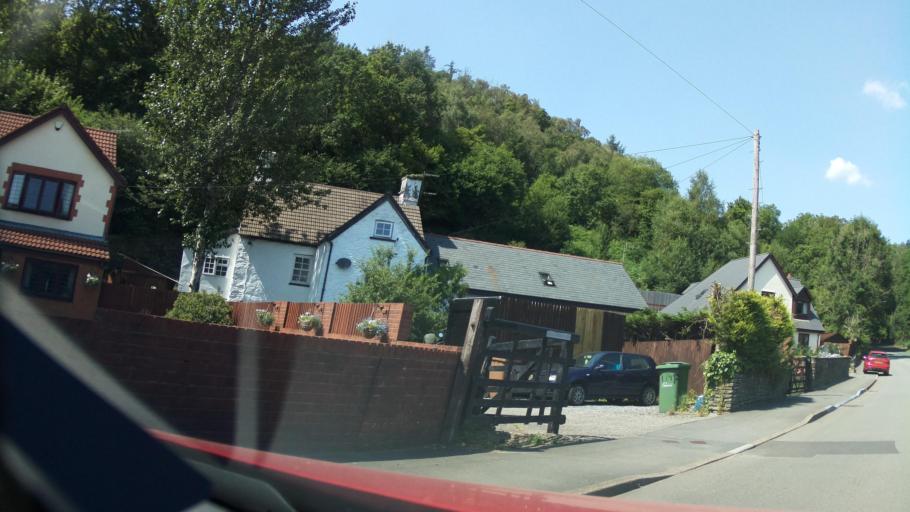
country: GB
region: Wales
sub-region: Caerphilly County Borough
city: Llanbradach
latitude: 51.6169
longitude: -3.2264
